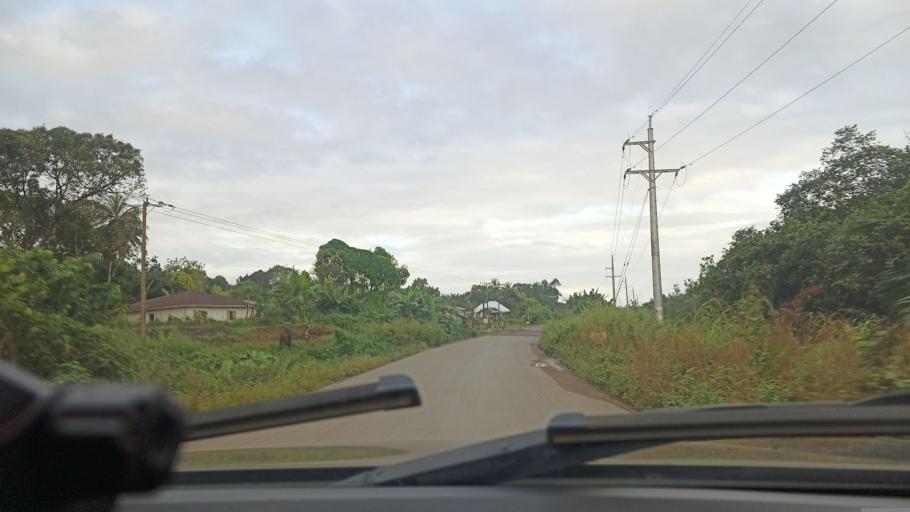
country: LR
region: Montserrado
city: Monrovia
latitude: 6.5624
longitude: -10.8719
